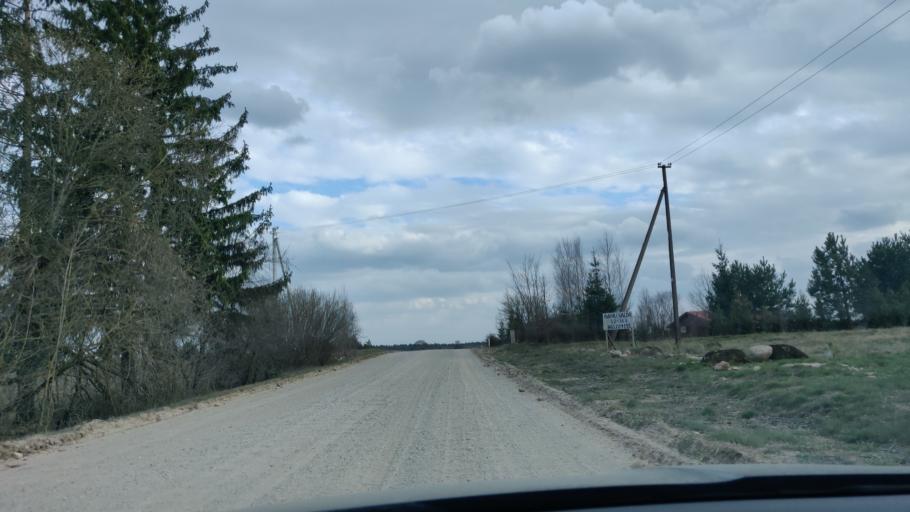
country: LT
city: Lentvaris
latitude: 54.6152
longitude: 25.0682
